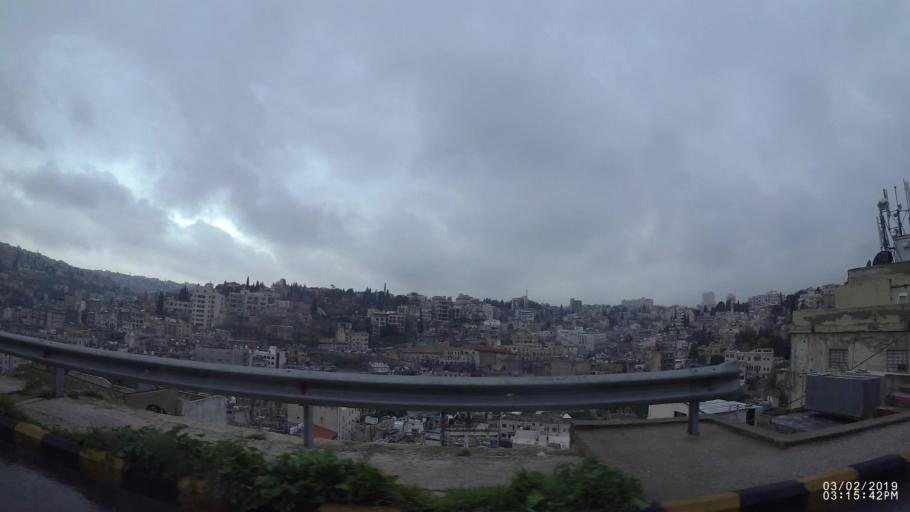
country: JO
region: Amman
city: Amman
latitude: 31.9534
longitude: 35.9337
